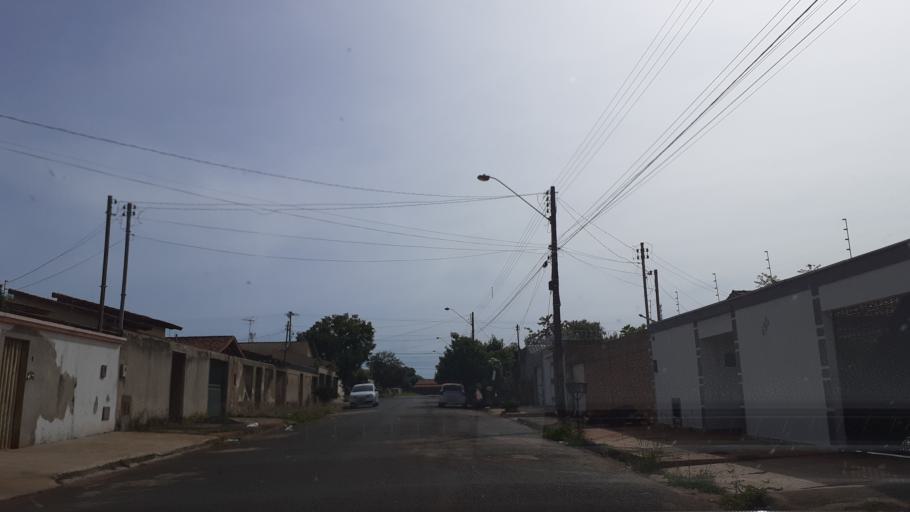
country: BR
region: Goias
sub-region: Itumbiara
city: Itumbiara
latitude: -18.4213
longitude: -49.2448
